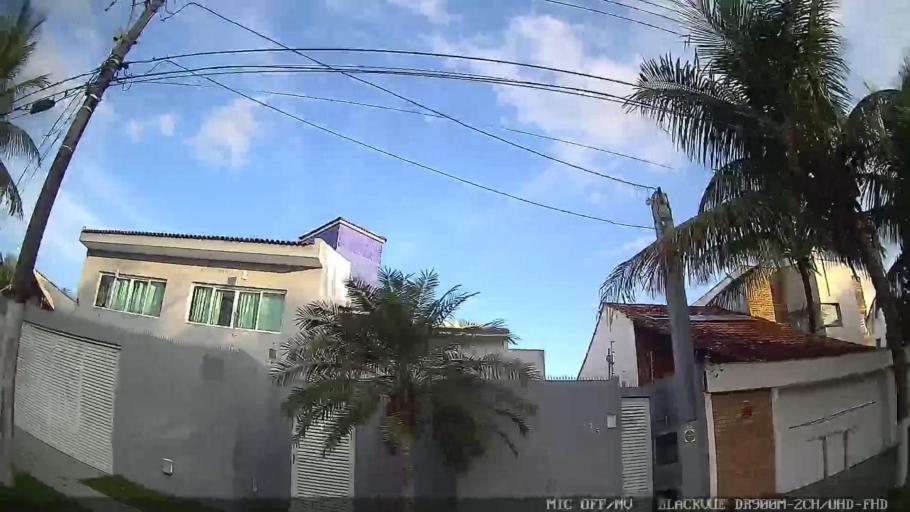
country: BR
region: Sao Paulo
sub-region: Guaruja
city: Guaruja
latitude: -23.9828
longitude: -46.2185
